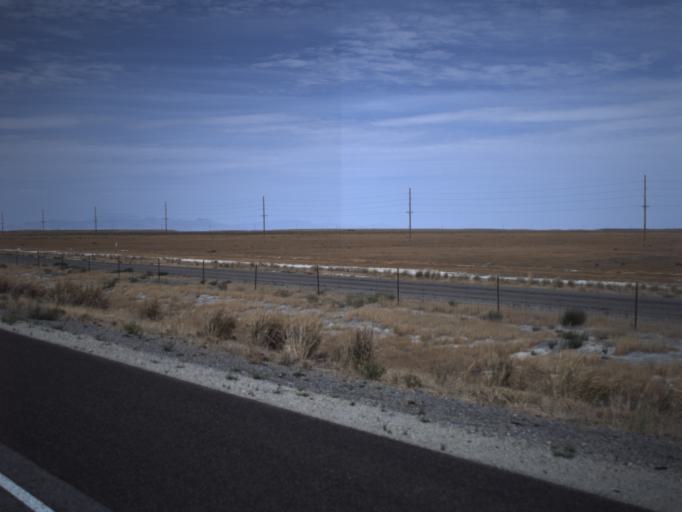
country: US
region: Utah
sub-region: Tooele County
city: Grantsville
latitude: 40.7264
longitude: -113.1789
